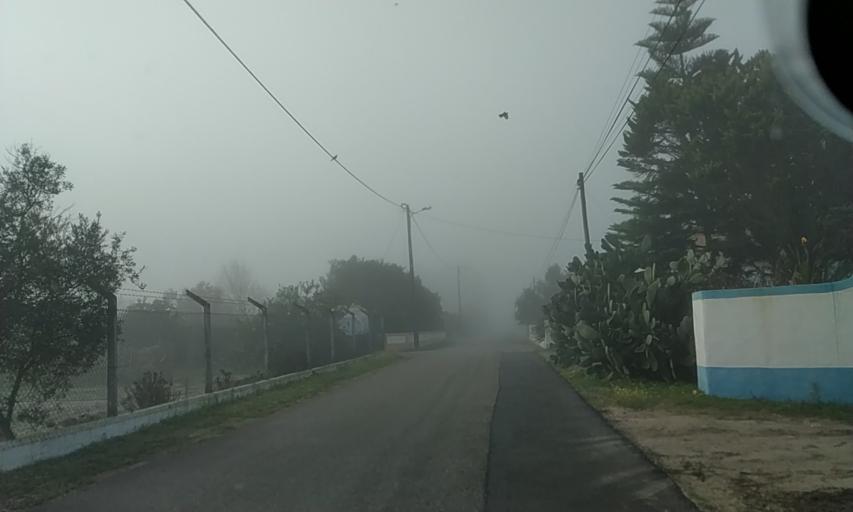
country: PT
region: Setubal
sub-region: Palmela
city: Pinhal Novo
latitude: 38.6095
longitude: -8.8838
